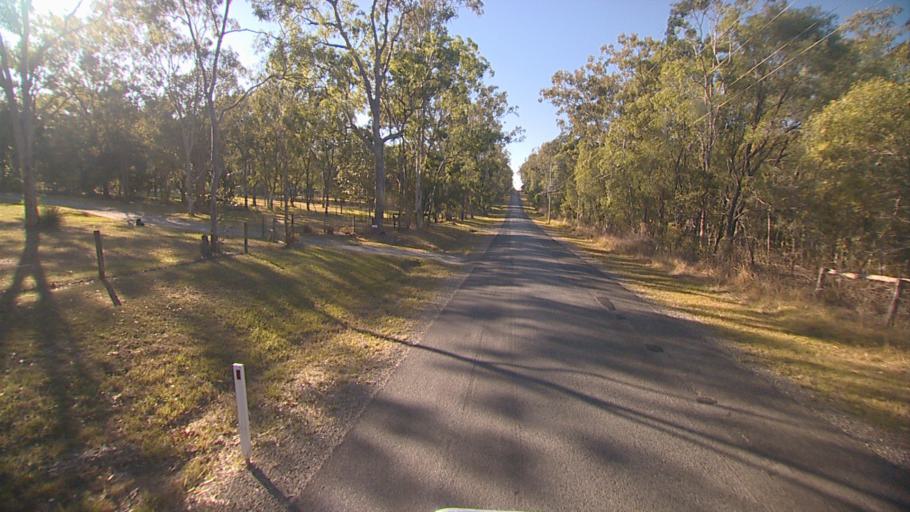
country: AU
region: Queensland
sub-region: Logan
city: North Maclean
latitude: -27.7889
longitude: 152.9748
